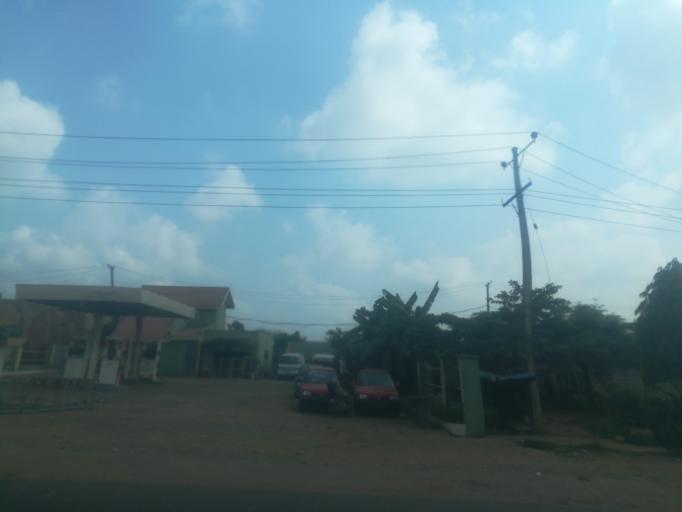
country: NG
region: Oyo
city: Ibadan
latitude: 7.4221
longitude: 3.9376
